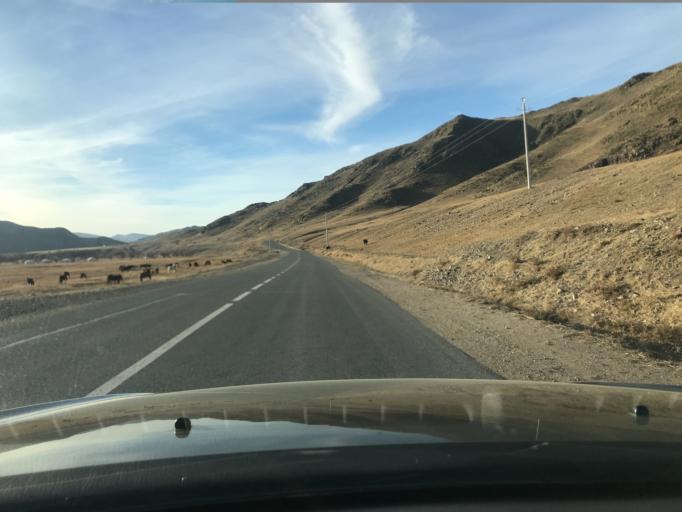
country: MN
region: Central Aimak
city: Dzuunmod
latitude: 47.8230
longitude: 107.3552
